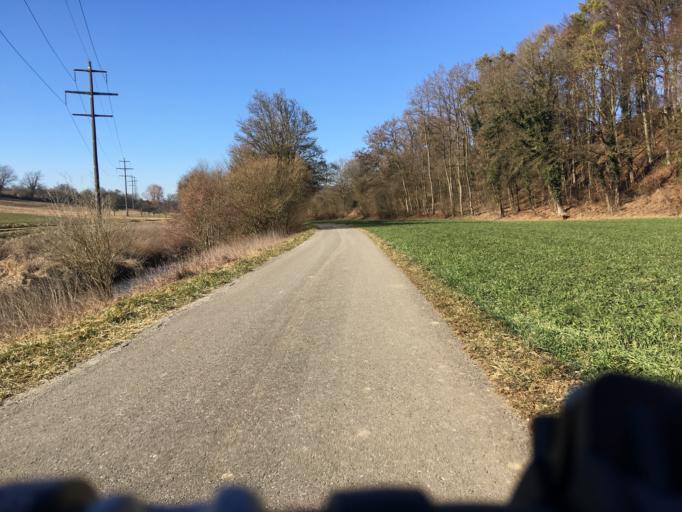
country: CH
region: Schaffhausen
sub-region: Bezirk Reiat
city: Thayngen
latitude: 47.7328
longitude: 8.7355
